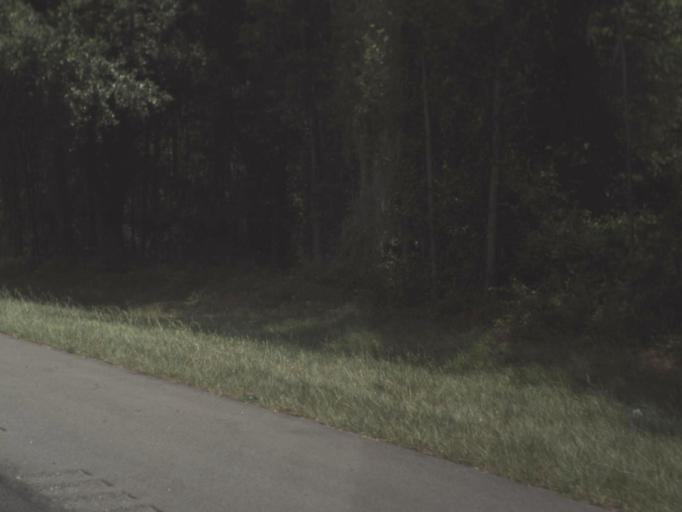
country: US
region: Florida
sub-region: Hamilton County
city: Jasper
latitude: 30.5555
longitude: -83.0834
